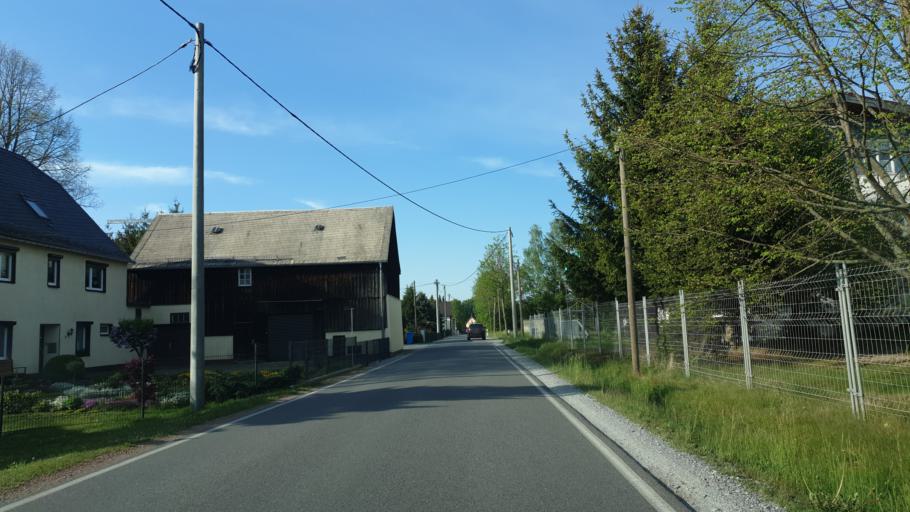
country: DE
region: Saxony
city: Jahnsdorf
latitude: 50.7589
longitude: 12.8607
